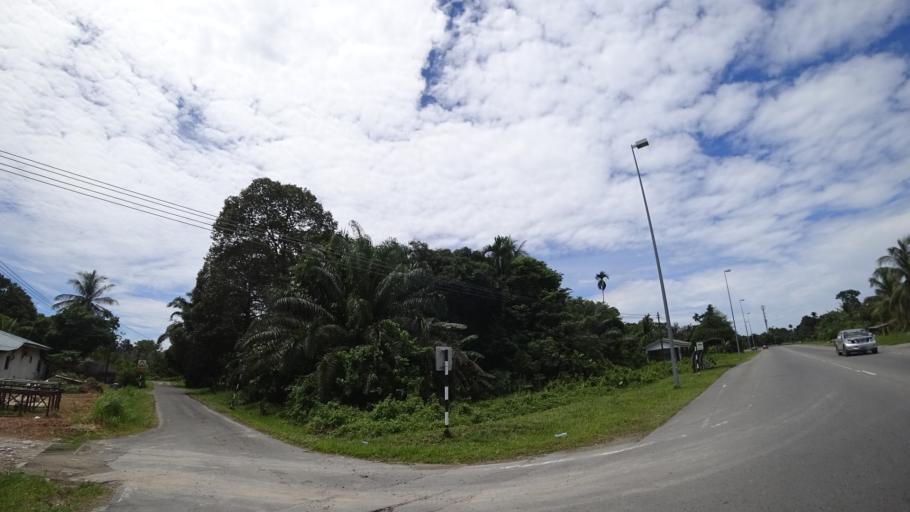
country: BN
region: Brunei and Muara
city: Bandar Seri Begawan
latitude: 4.8128
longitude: 114.8358
